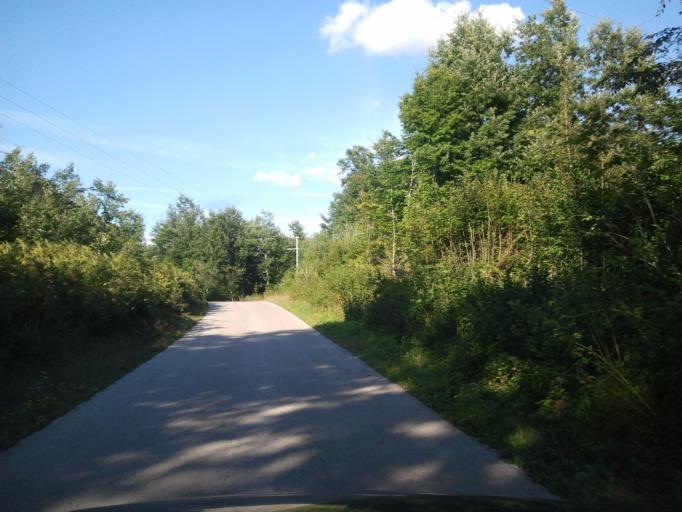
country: HR
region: Zadarska
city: Obrovac
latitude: 44.3538
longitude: 15.6875
